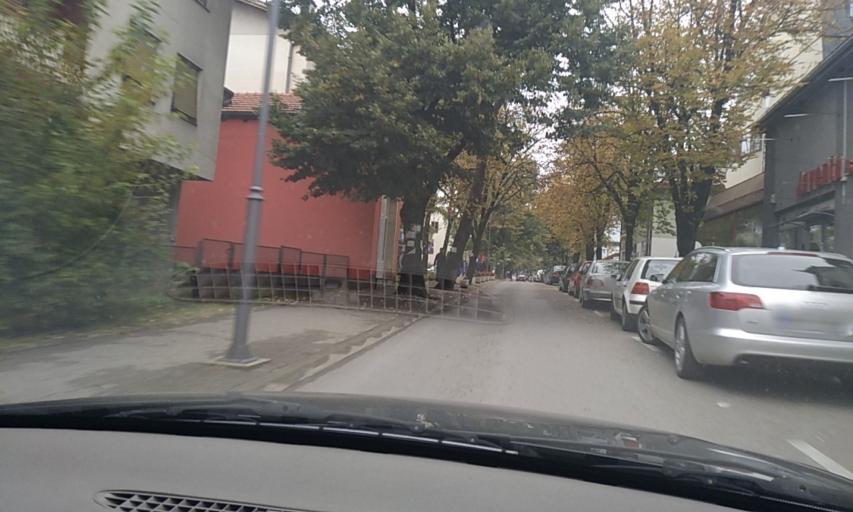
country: BA
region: Republika Srpska
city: Prnjavor
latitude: 44.8689
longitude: 17.6634
